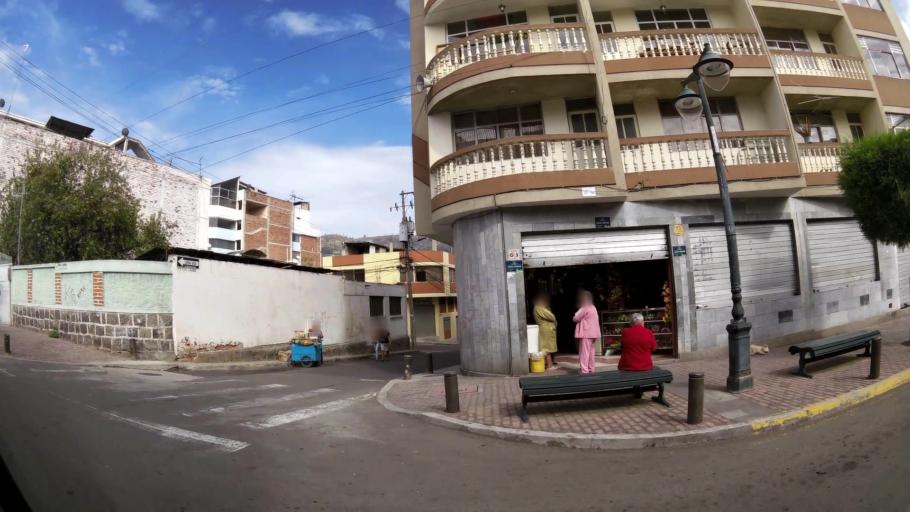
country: EC
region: Tungurahua
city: Ambato
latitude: -1.2435
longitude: -78.6359
